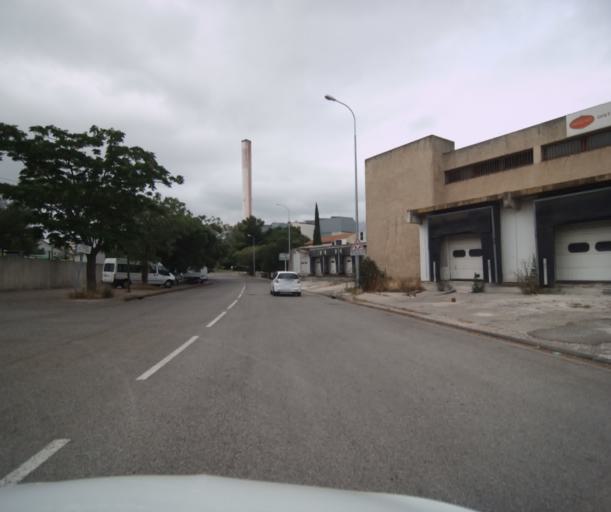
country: FR
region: Provence-Alpes-Cote d'Azur
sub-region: Departement du Var
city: La Seyne-sur-Mer
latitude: 43.1235
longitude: 5.8919
